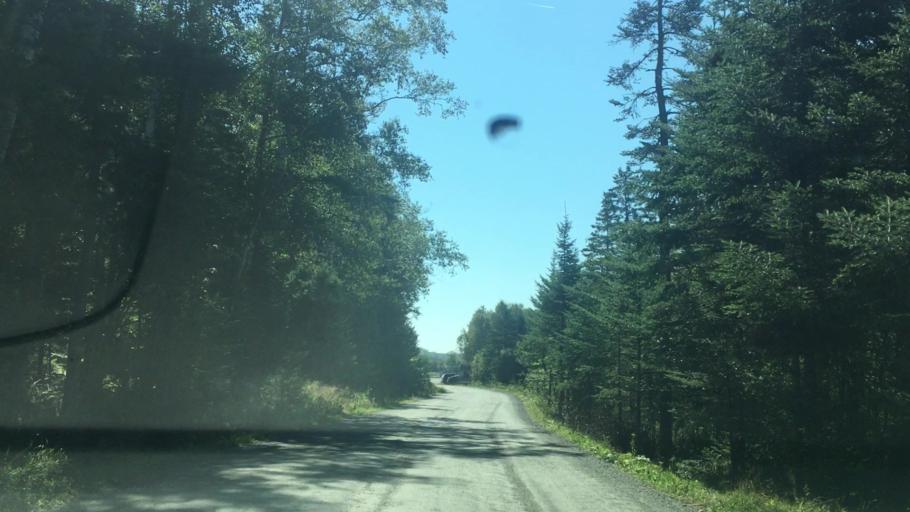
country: CA
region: Nova Scotia
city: Antigonish
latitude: 45.1399
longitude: -61.9829
